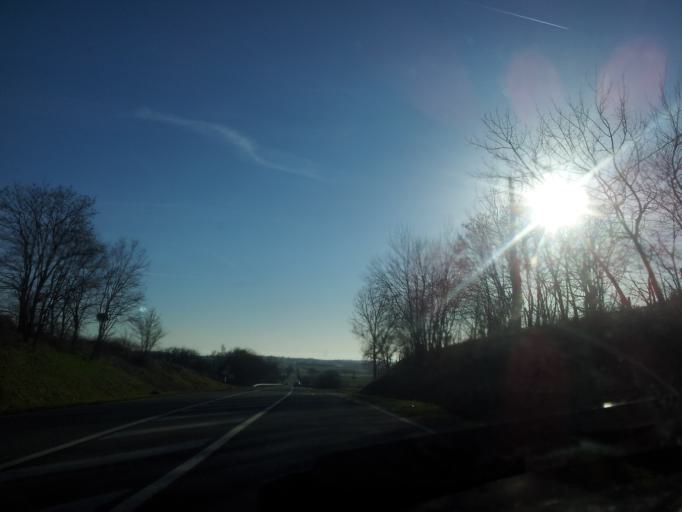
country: FR
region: Auvergne
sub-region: Departement de l'Allier
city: Chantelle
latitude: 46.3171
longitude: 3.1329
